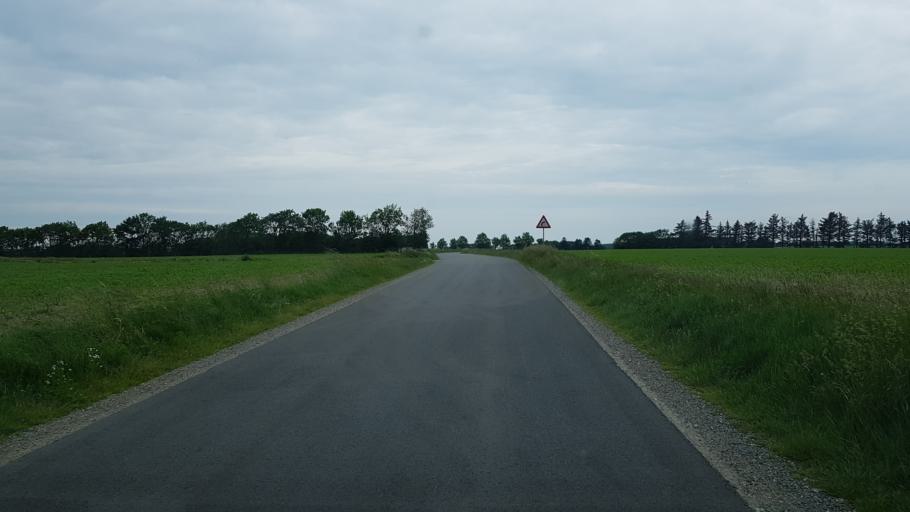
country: DK
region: South Denmark
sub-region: Varde Kommune
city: Oksbol
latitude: 55.7319
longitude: 8.3718
